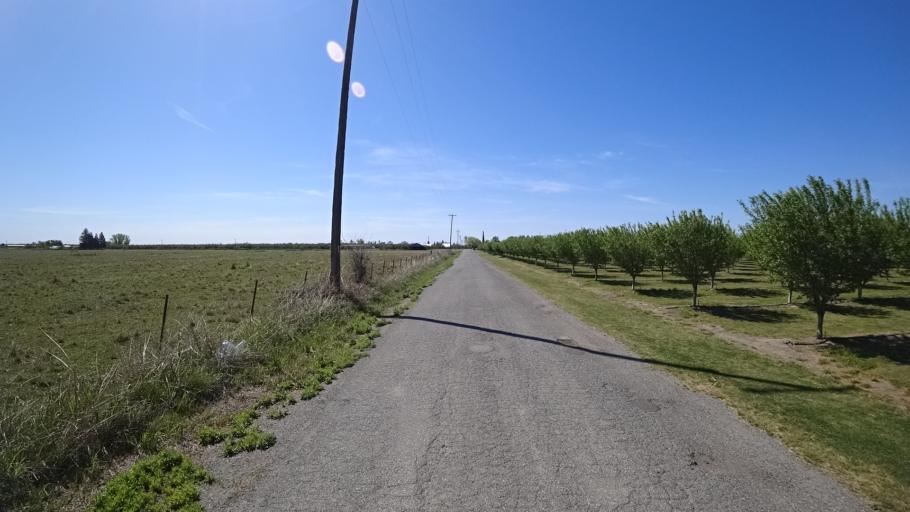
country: US
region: California
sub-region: Glenn County
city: Orland
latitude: 39.7422
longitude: -122.1138
